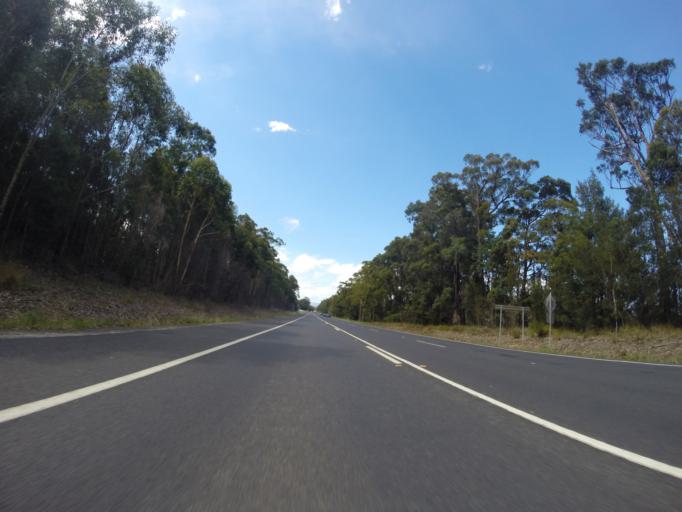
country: AU
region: New South Wales
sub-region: Shoalhaven Shire
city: Falls Creek
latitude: -35.0227
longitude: 150.5789
